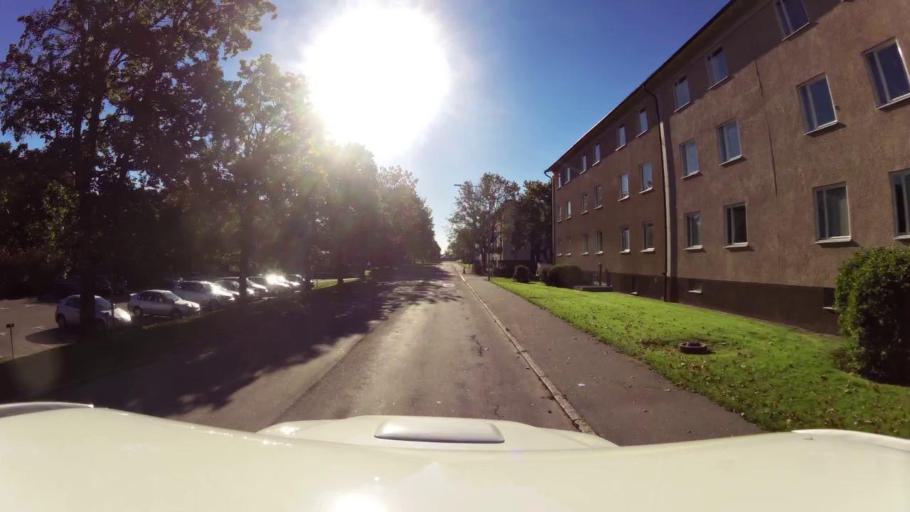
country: SE
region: OEstergoetland
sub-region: Linkopings Kommun
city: Linkoping
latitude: 58.4121
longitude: 15.6532
